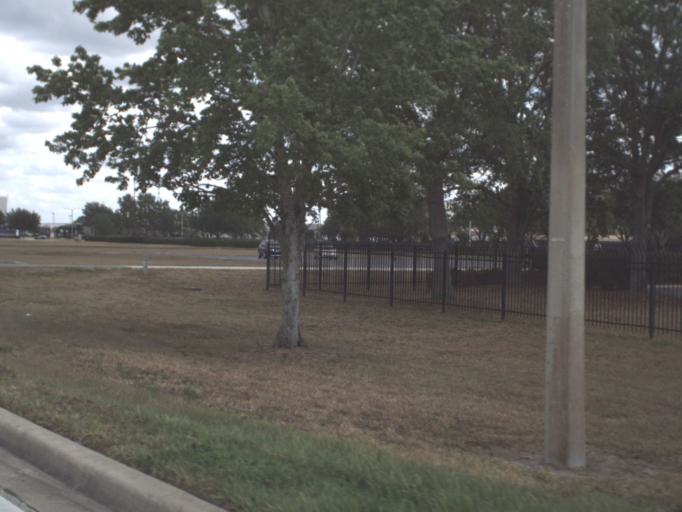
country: US
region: Florida
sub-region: Orange County
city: Taft
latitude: 28.4193
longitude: -81.3338
